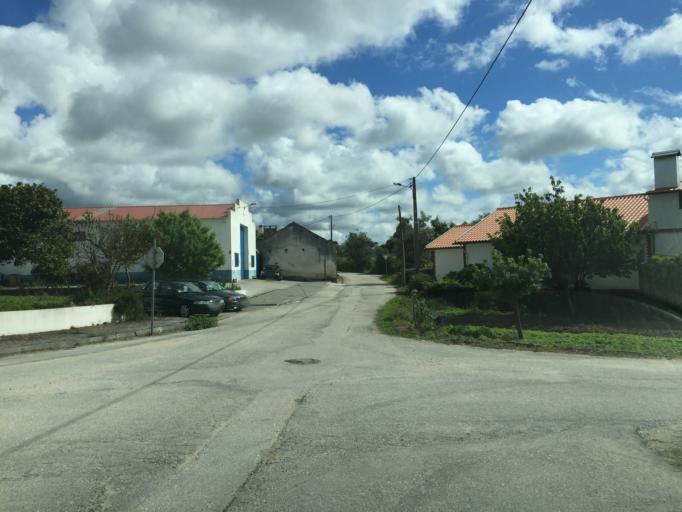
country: PT
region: Leiria
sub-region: Pombal
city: Lourical
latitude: 39.9852
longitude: -8.8056
